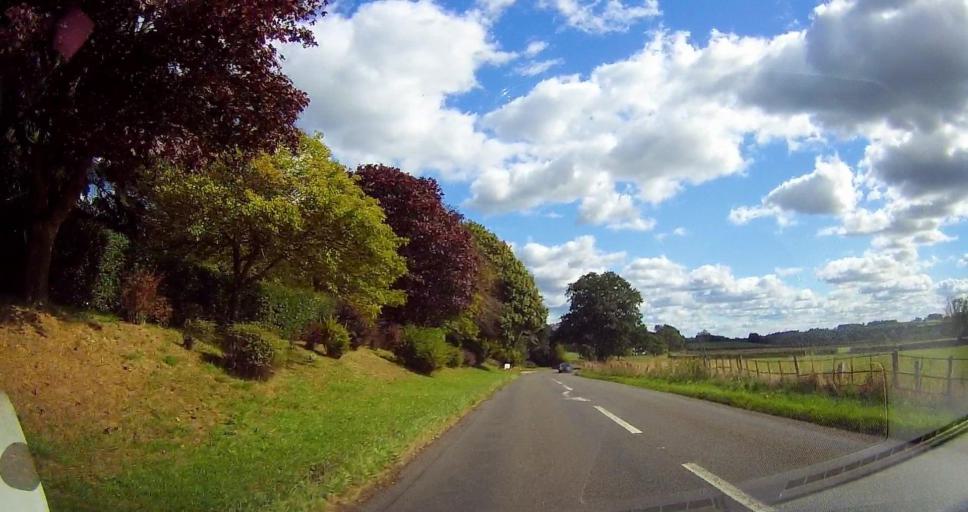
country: GB
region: England
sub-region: Staffordshire
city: Standon
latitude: 52.9553
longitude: -2.3688
